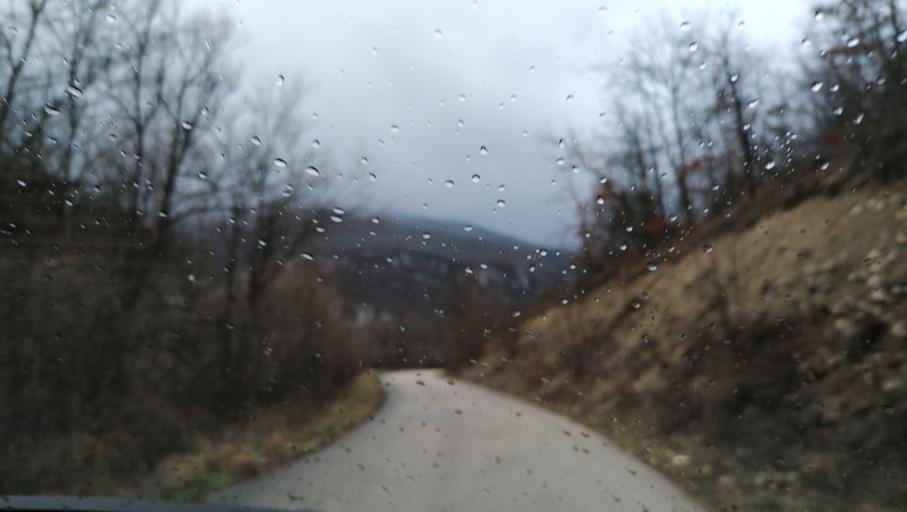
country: RS
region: Central Serbia
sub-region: Pirotski Okrug
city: Dimitrovgrad
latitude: 42.9810
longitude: 22.6479
